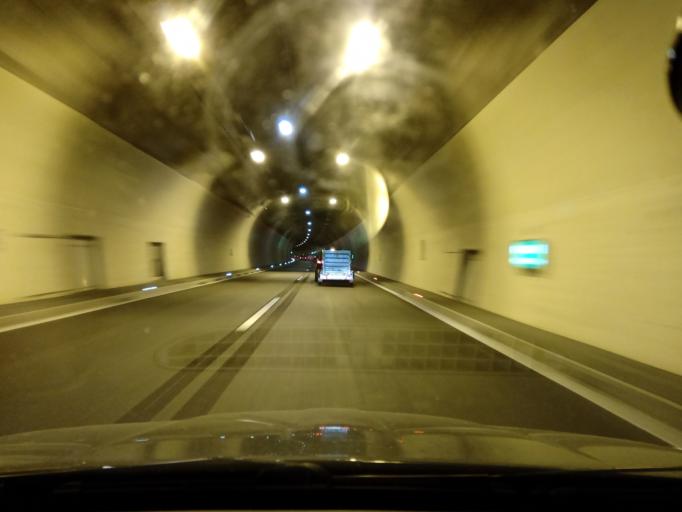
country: AT
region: Styria
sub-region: Politischer Bezirk Bruck-Muerzzuschlag
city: Bruck an der Mur
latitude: 47.4024
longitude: 15.2587
